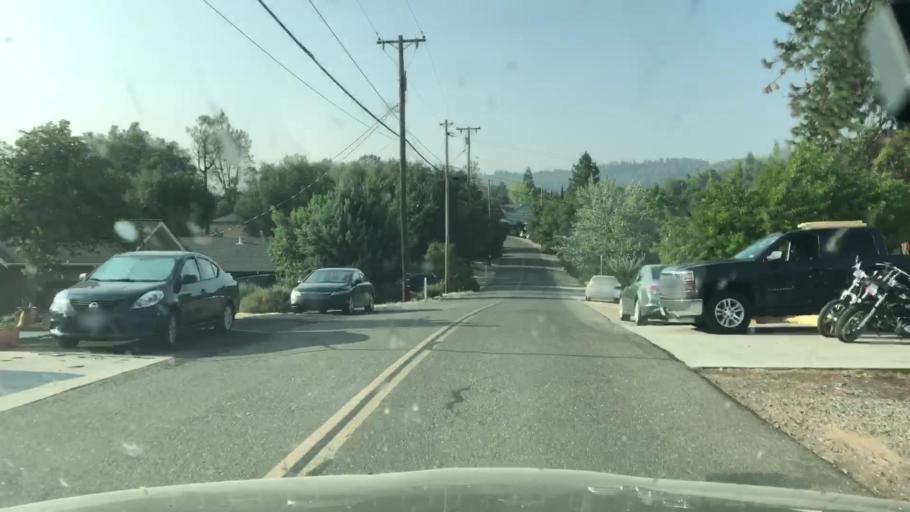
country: US
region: California
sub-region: Lake County
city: Hidden Valley Lake
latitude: 38.8166
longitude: -122.5707
